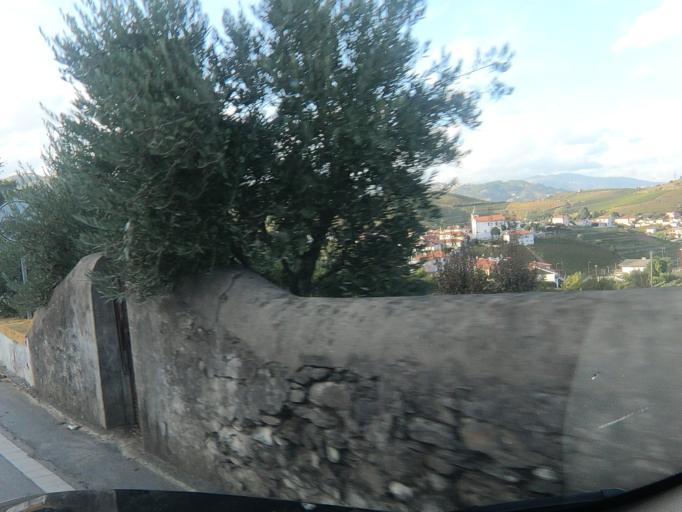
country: PT
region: Vila Real
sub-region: Santa Marta de Penaguiao
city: Santa Marta de Penaguiao
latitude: 41.2024
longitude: -7.7773
